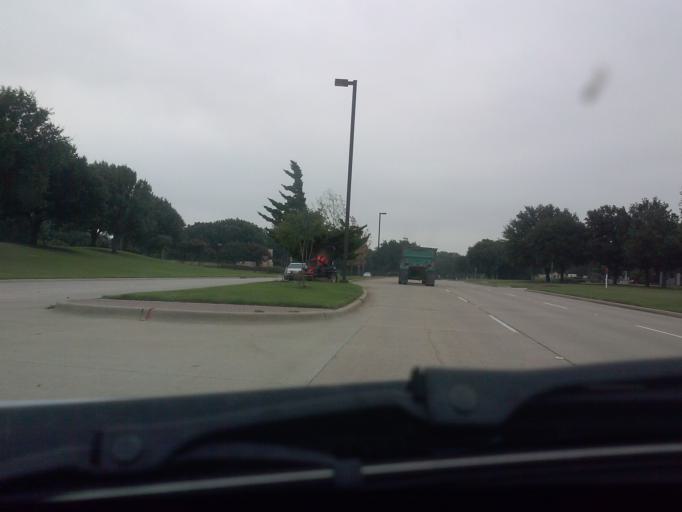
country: US
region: Texas
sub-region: Denton County
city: The Colony
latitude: 33.0705
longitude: -96.8146
